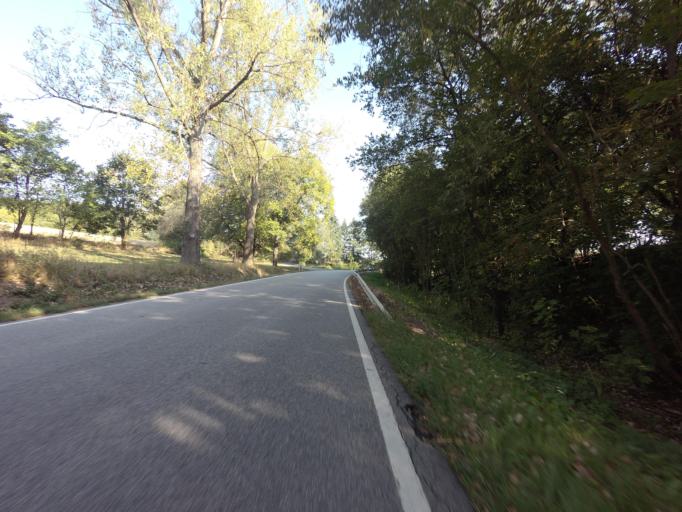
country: CZ
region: Jihocesky
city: Tyn nad Vltavou
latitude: 49.2388
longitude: 14.4200
